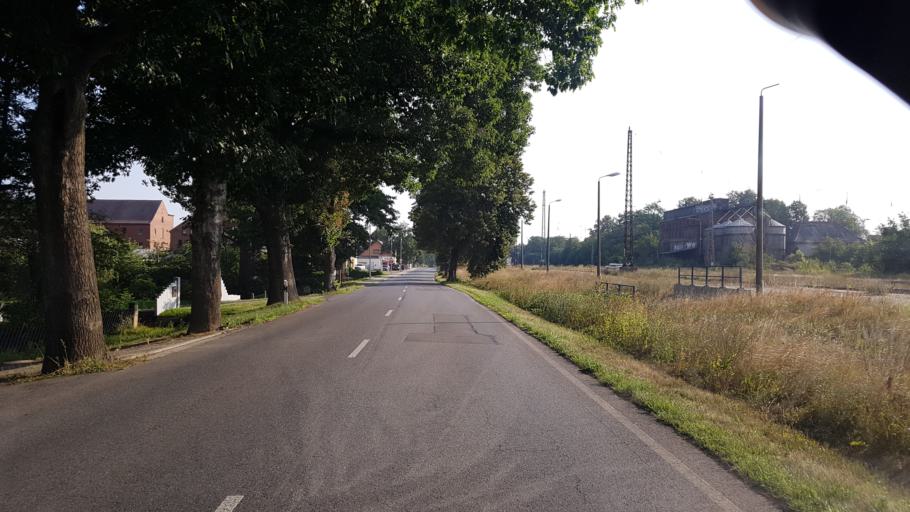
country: DE
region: Brandenburg
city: Drebkau
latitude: 51.6515
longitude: 14.2179
